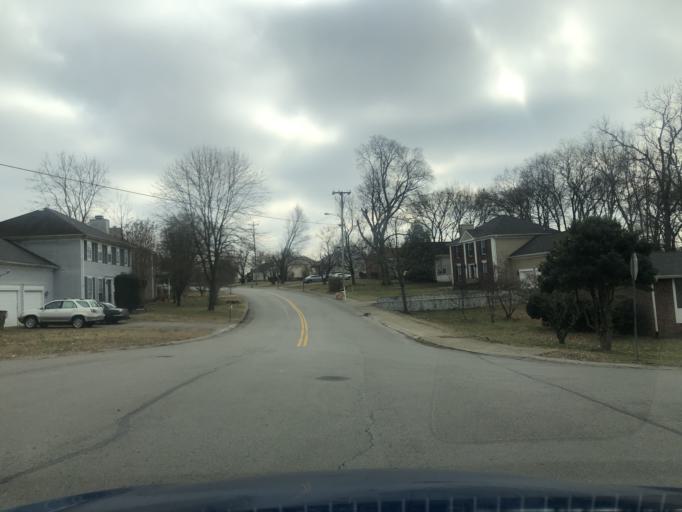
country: US
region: Tennessee
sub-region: Davidson County
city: Oak Hill
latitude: 36.0922
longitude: -86.7102
